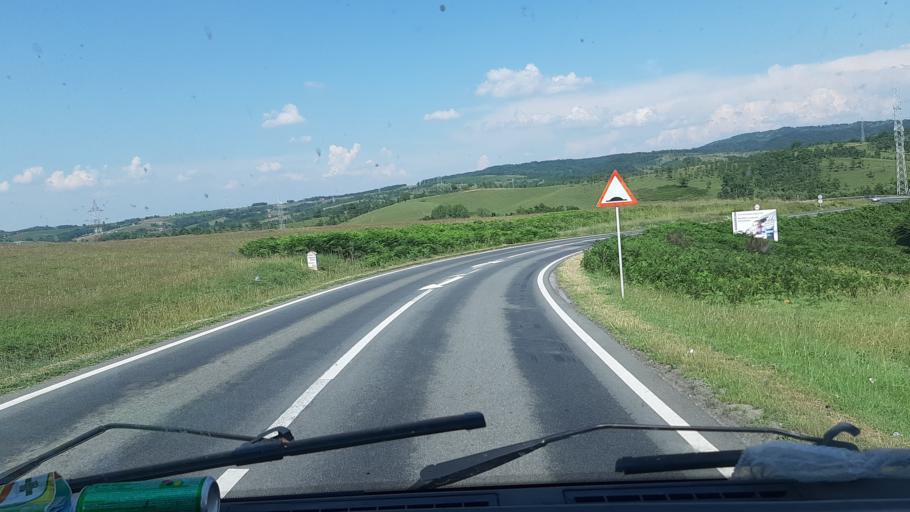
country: RO
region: Caras-Severin
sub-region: Comuna Ezeris
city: Ezeris
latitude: 45.3703
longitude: 21.9307
